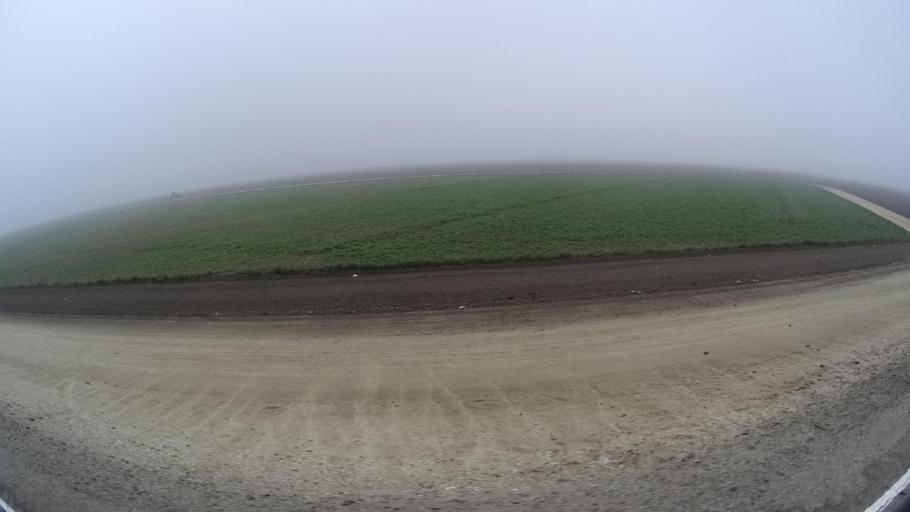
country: US
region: California
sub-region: Kern County
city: Buttonwillow
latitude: 35.4376
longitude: -119.5476
